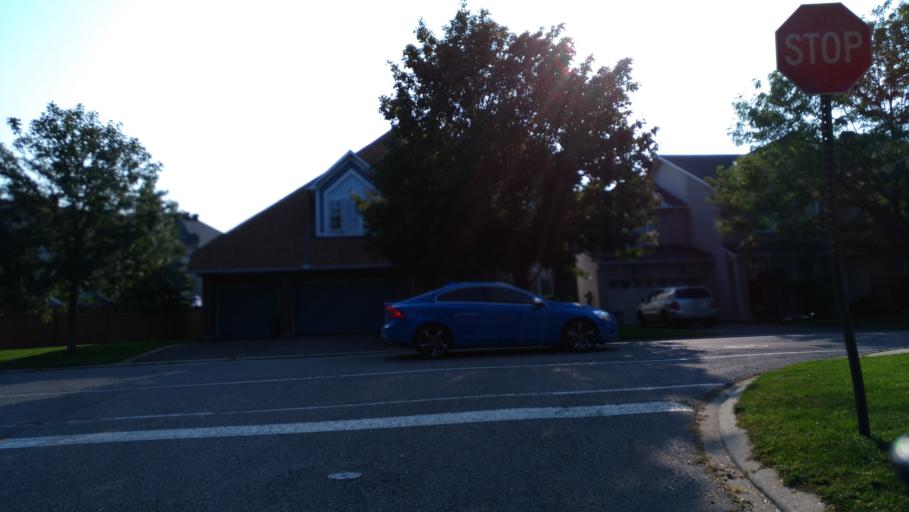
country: CA
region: Ontario
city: Bells Corners
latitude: 45.3512
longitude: -75.9303
